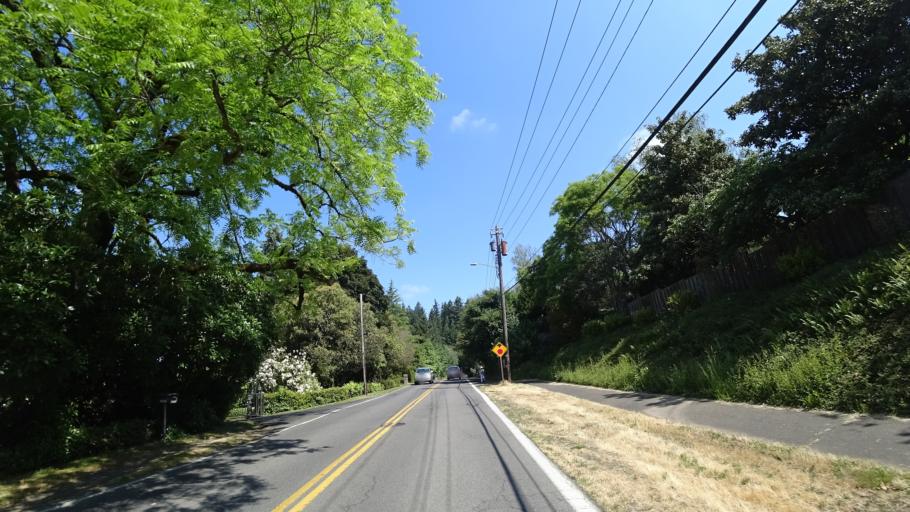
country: US
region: Oregon
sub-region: Washington County
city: Durham
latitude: 45.4245
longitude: -122.7221
